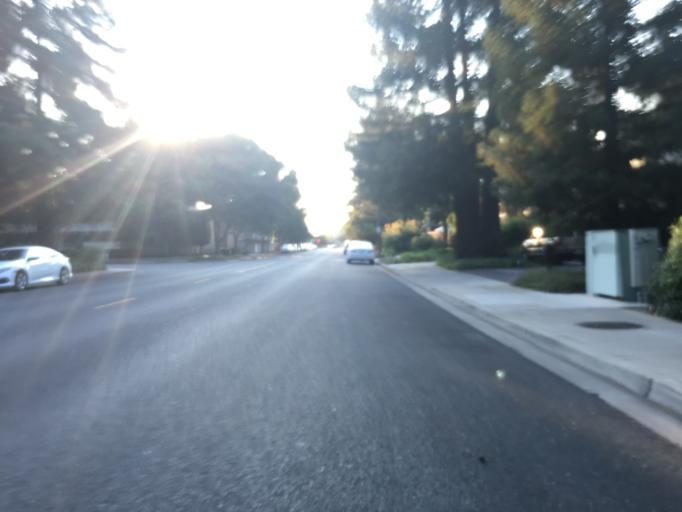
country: US
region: California
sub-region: Santa Clara County
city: Mountain View
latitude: 37.3966
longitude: -122.0738
